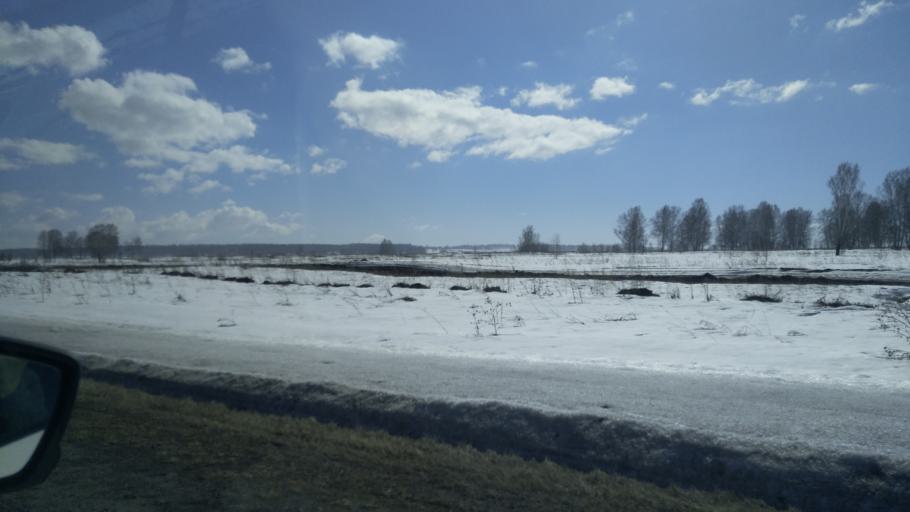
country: RU
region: Kemerovo
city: Yurga
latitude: 55.6856
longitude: 85.0789
